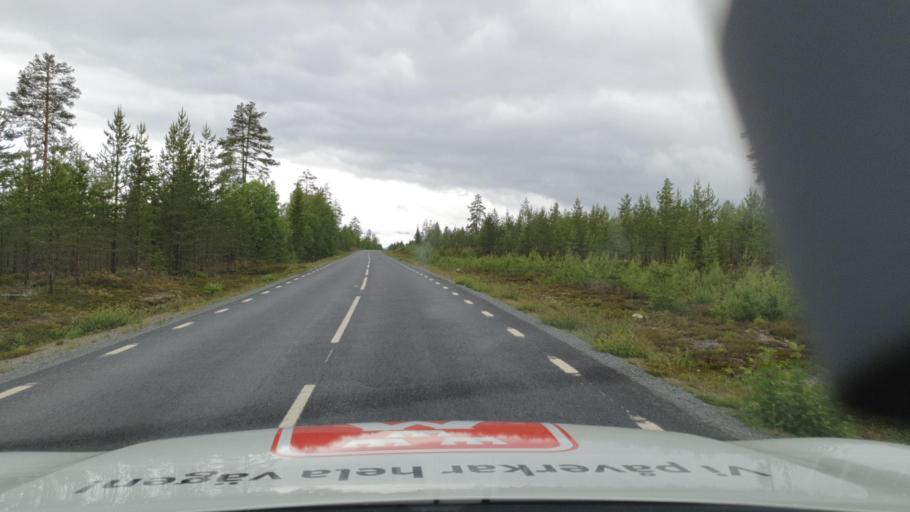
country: SE
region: Vaesterbotten
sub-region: Dorotea Kommun
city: Dorotea
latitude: 64.2062
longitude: 16.5618
